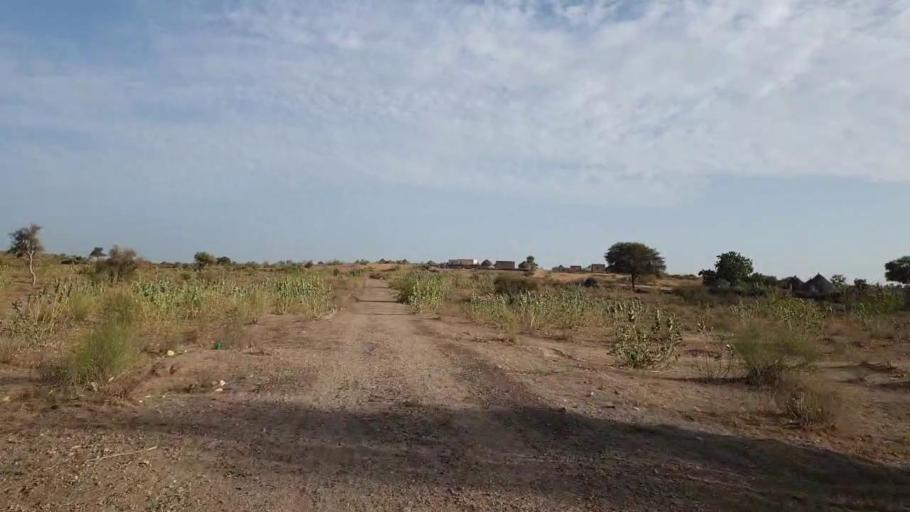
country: PK
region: Sindh
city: Nabisar
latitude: 25.0842
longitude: 69.9889
